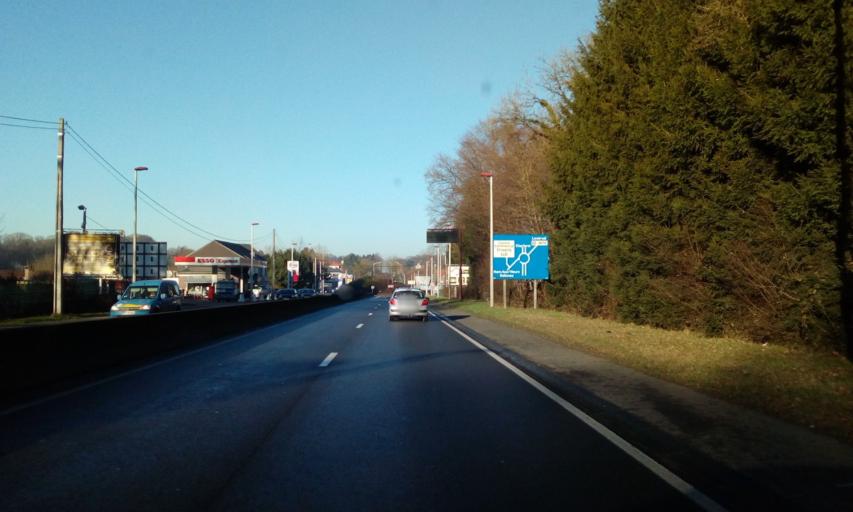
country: BE
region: Wallonia
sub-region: Province du Hainaut
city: Charleroi
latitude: 50.3595
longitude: 4.4702
